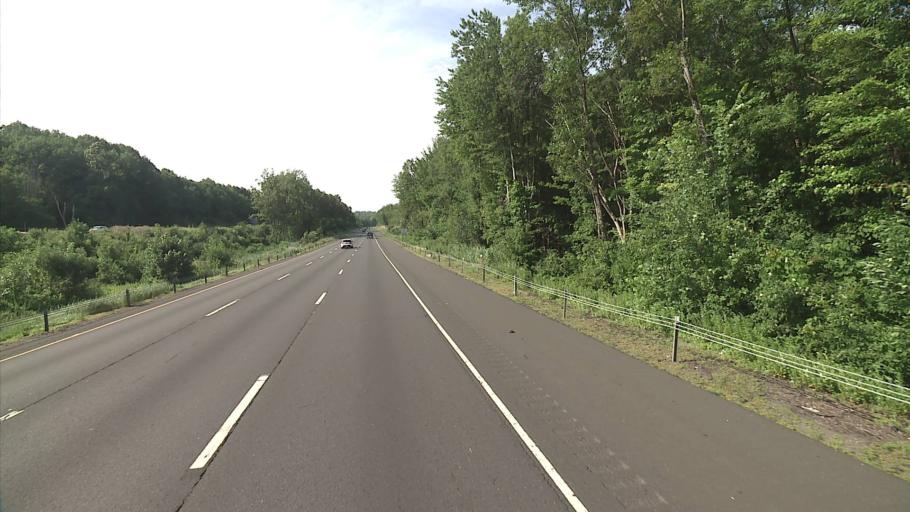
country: US
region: Connecticut
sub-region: Middlesex County
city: Cromwell
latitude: 41.5954
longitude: -72.7093
